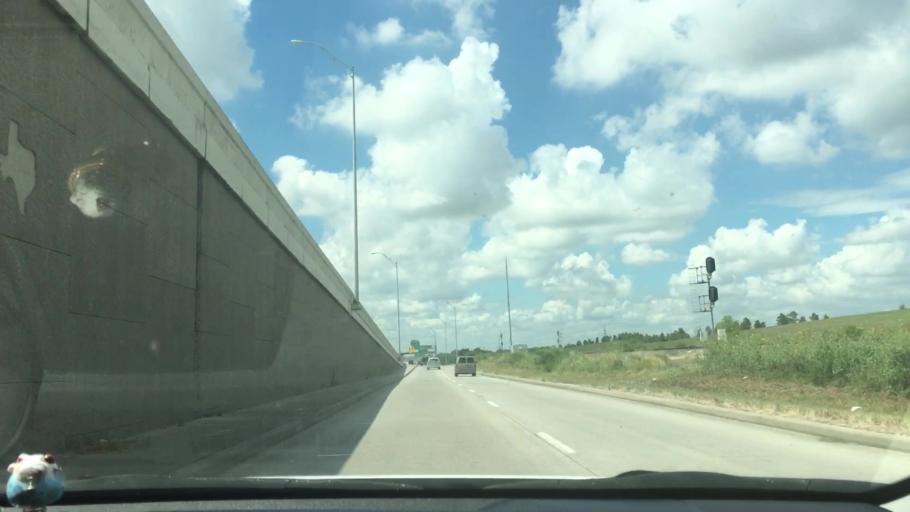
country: US
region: Texas
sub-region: Harris County
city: Bellaire
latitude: 29.6462
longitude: -95.4673
